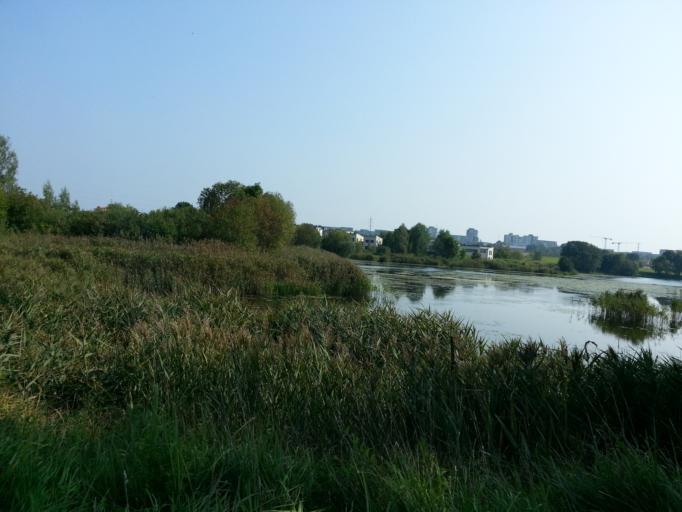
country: LT
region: Vilnius County
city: Justiniskes
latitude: 54.7230
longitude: 25.1972
